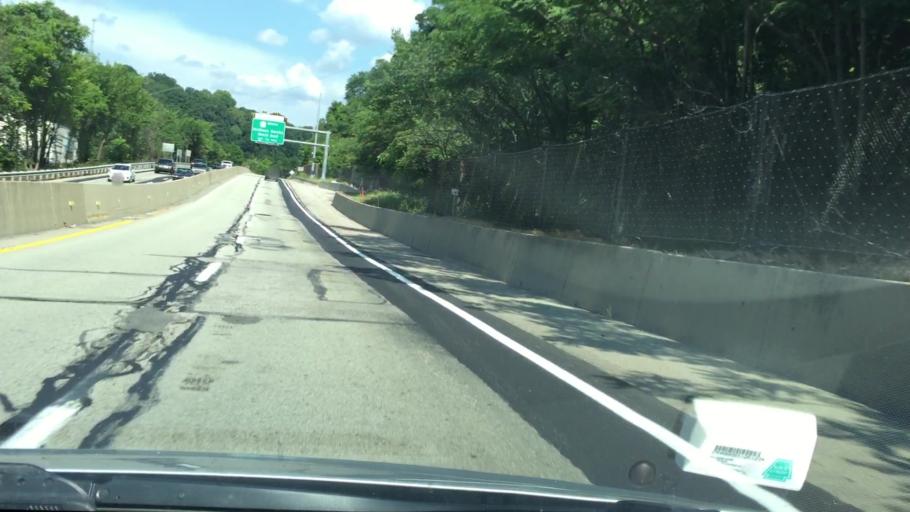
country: US
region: Pennsylvania
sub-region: Allegheny County
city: Green Tree
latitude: 40.4336
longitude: -80.0289
